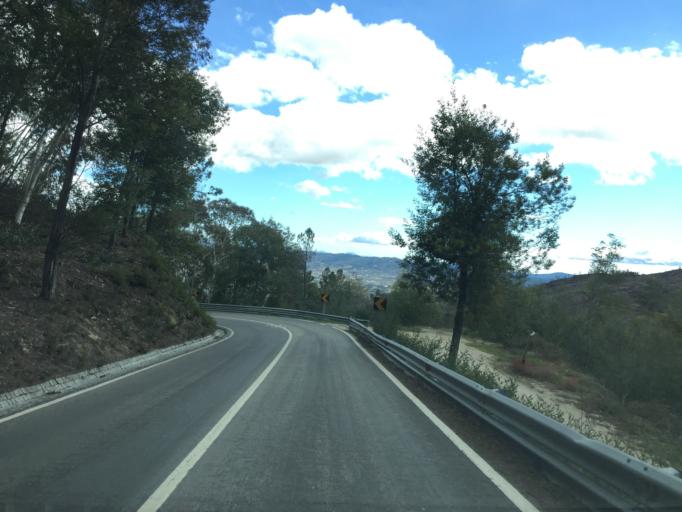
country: PT
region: Castelo Branco
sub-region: Covilha
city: Covilha
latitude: 40.2810
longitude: -7.5248
